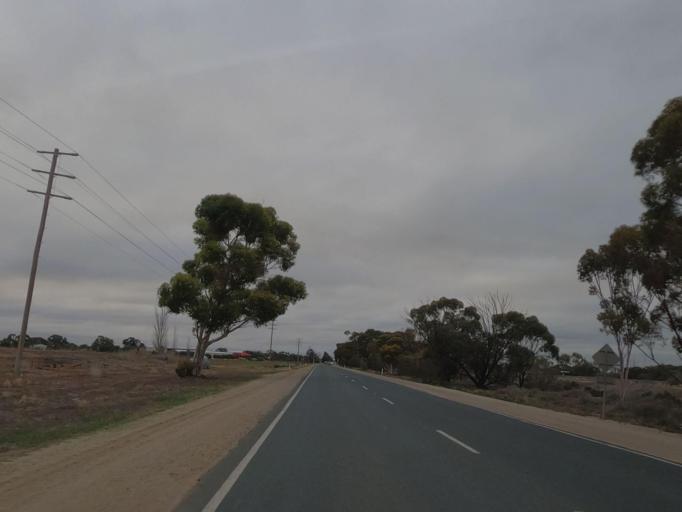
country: AU
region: Victoria
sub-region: Swan Hill
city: Swan Hill
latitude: -35.3926
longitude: 143.5711
